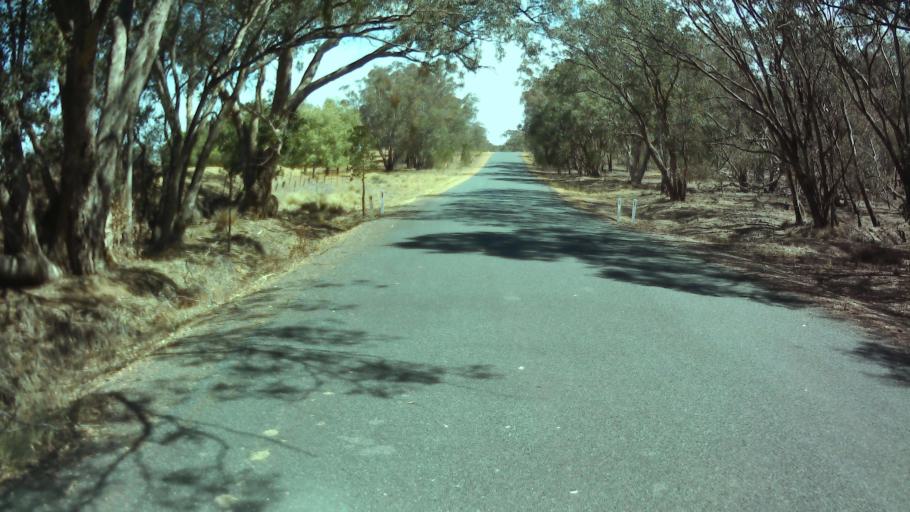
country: AU
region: New South Wales
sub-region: Weddin
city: Grenfell
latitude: -34.0025
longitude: 148.1308
